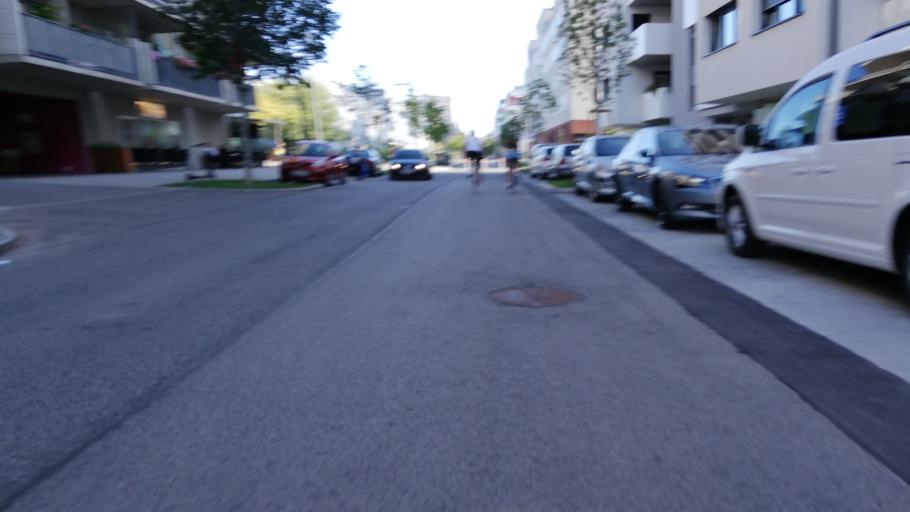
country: AT
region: Vienna
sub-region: Wien Stadt
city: Vienna
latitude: 48.2264
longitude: 16.3939
